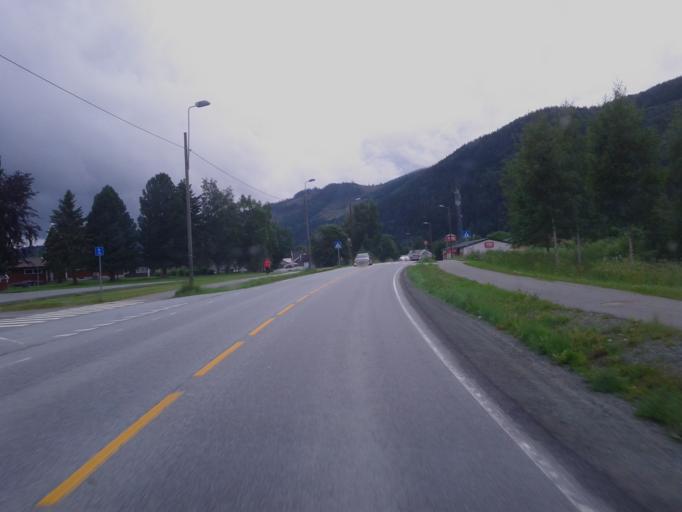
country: NO
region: Sor-Trondelag
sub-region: Melhus
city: Lundamo
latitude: 63.1522
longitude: 10.2861
